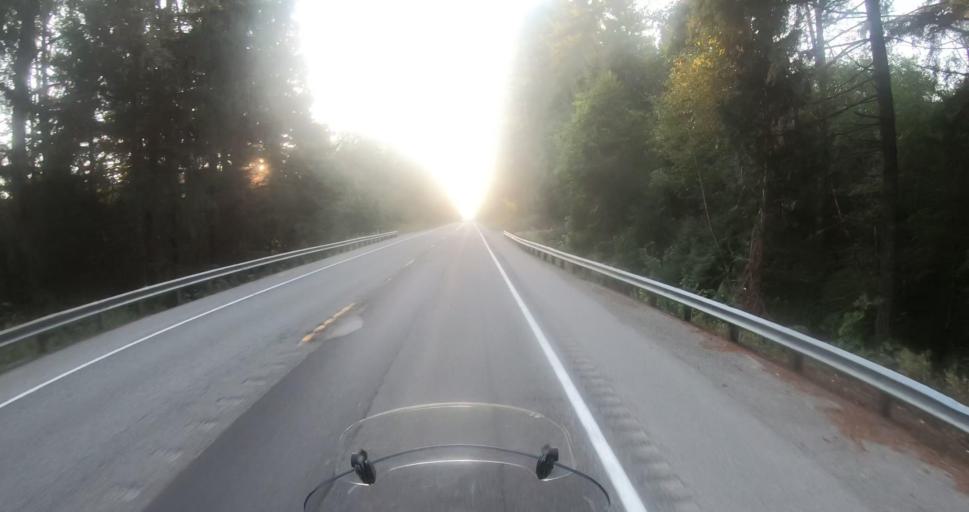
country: US
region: Washington
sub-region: Lewis County
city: Morton
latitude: 46.5379
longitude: -122.0223
